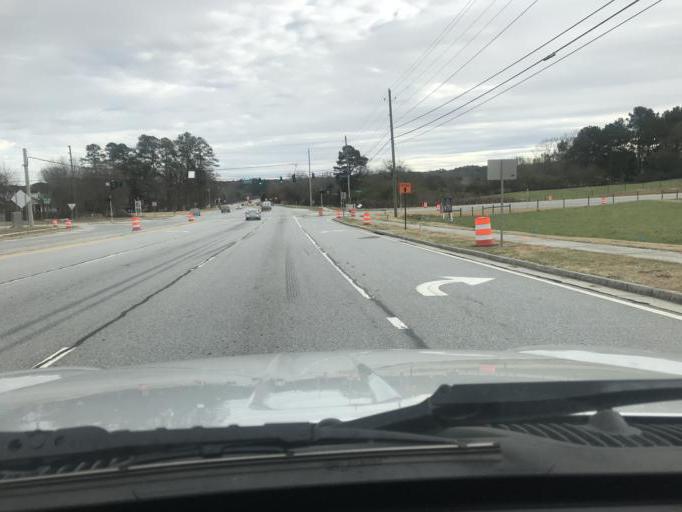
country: US
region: Georgia
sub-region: Gwinnett County
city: Buford
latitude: 34.0613
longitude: -83.9448
